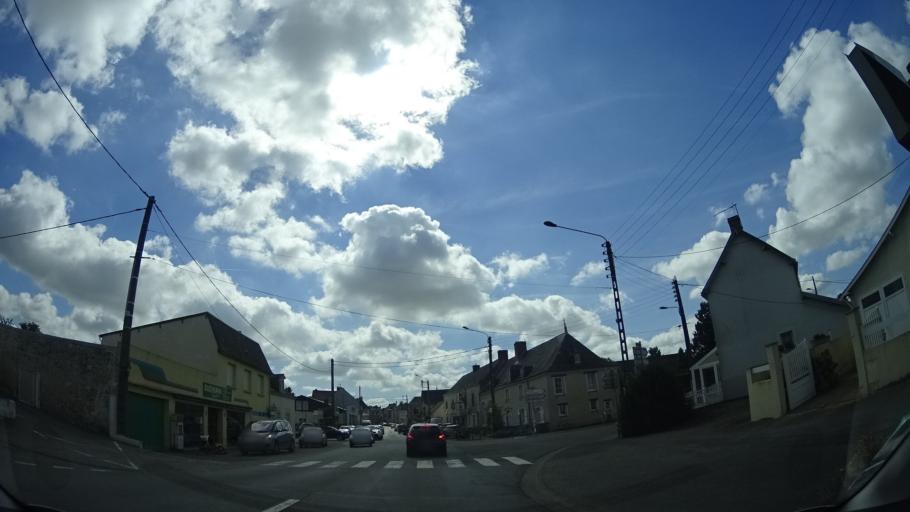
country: FR
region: Pays de la Loire
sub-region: Departement de la Mayenne
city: Meslay-du-Maine
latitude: 47.9521
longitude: -0.5572
